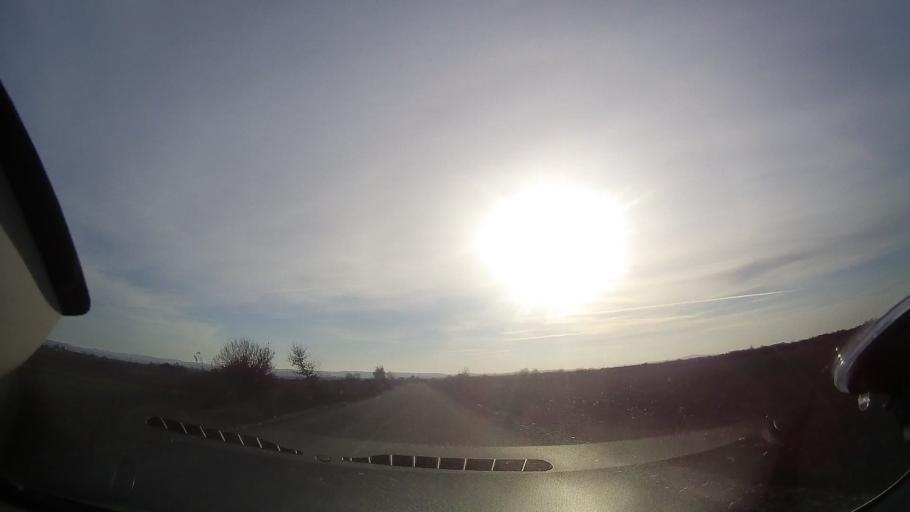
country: RO
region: Bihor
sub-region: Comuna Tileagd
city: Tileagd
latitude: 47.0889
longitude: 22.1770
